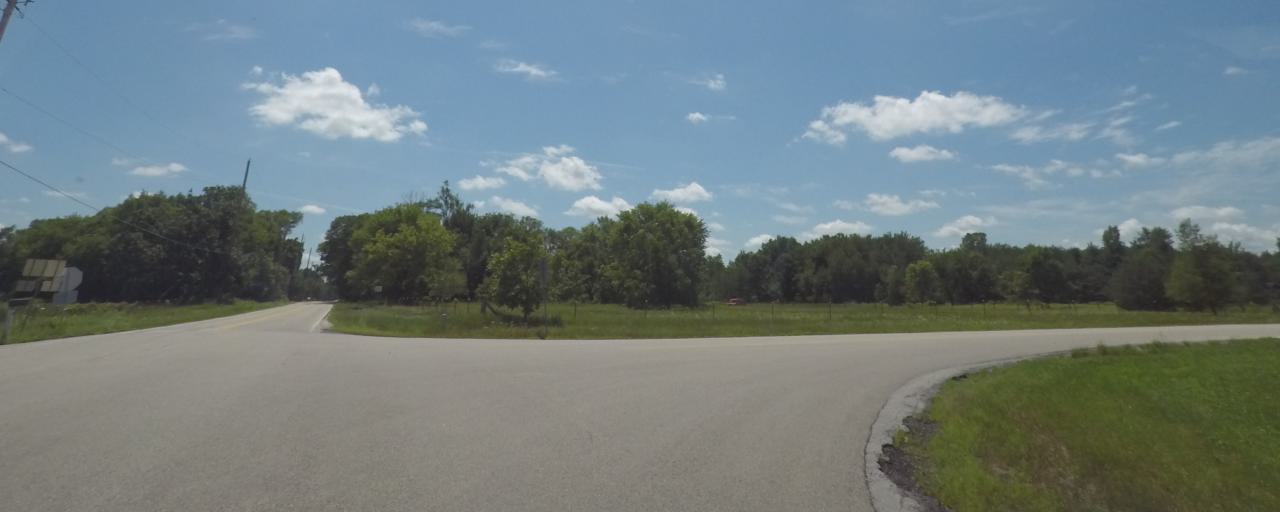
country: US
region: Wisconsin
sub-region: Waukesha County
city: Eagle
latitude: 42.9381
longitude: -88.4983
